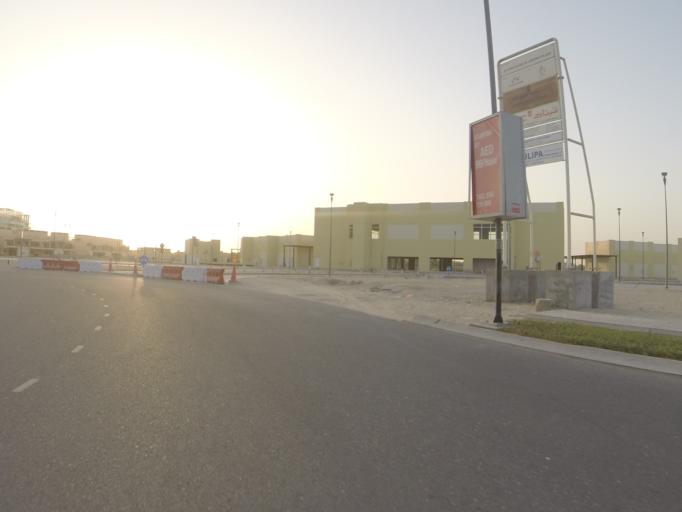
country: AE
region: Dubai
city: Dubai
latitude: 25.0647
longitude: 55.1459
